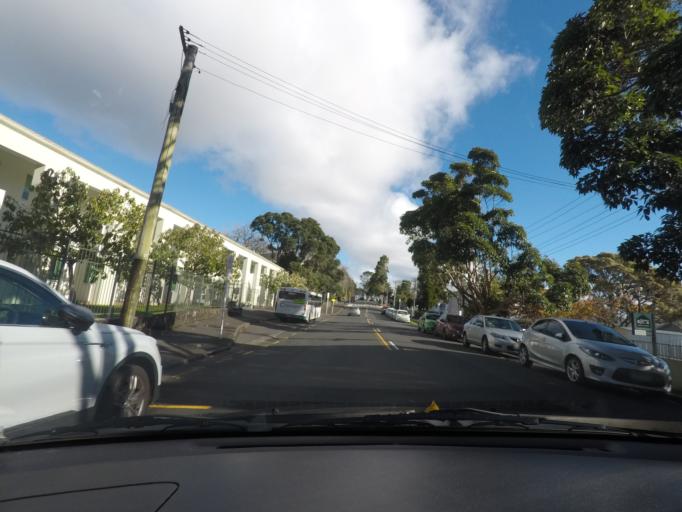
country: NZ
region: Auckland
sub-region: Auckland
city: Auckland
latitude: -36.8866
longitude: 174.7789
